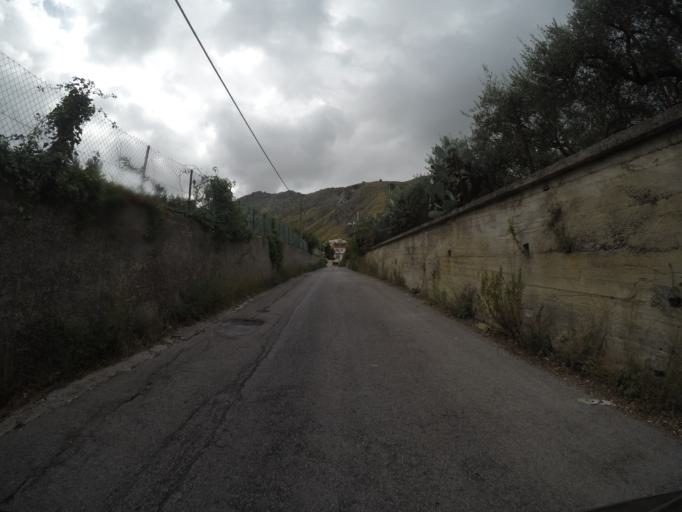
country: IT
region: Sicily
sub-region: Palermo
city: Carini
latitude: 38.1225
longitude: 13.1844
